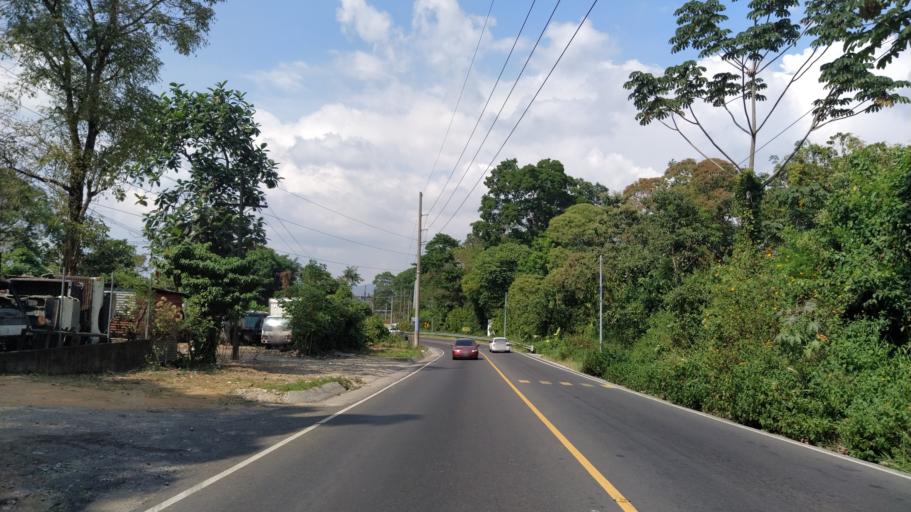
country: GT
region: Retalhuleu
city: San Felipe
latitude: 14.6202
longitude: -91.5883
